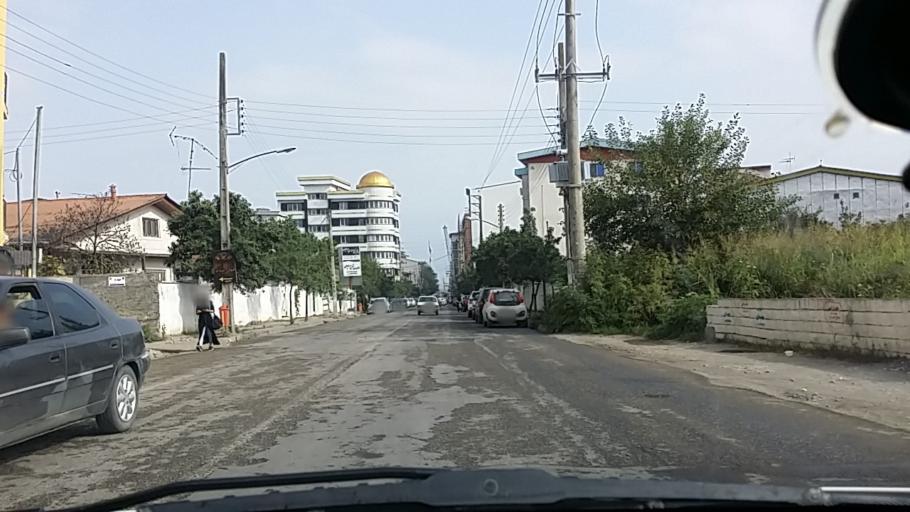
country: IR
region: Mazandaran
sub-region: Nowshahr
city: Nowshahr
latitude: 36.6475
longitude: 51.5085
